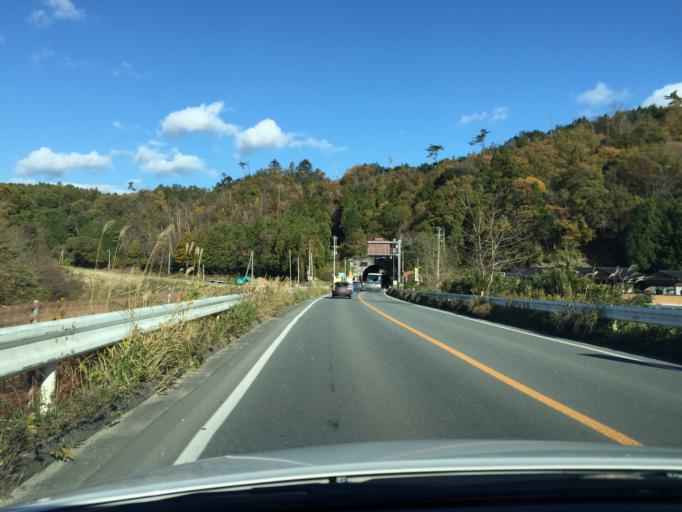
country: JP
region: Fukushima
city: Iwaki
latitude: 37.1596
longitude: 140.9952
